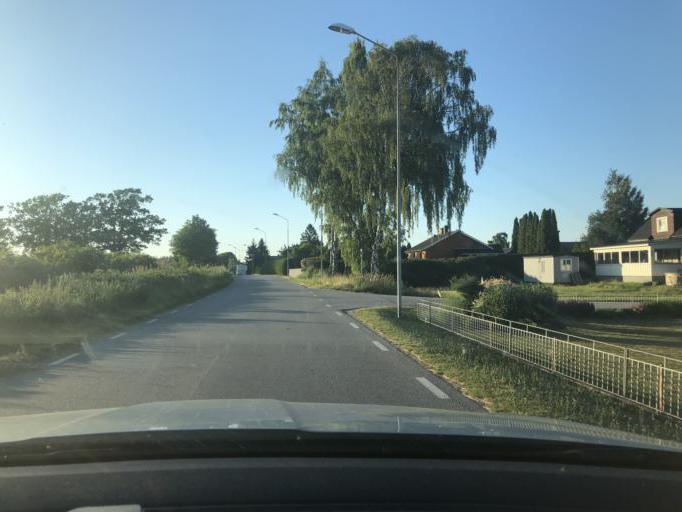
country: SE
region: Blekinge
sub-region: Karlshamns Kommun
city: Morrum
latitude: 56.1228
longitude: 14.6699
